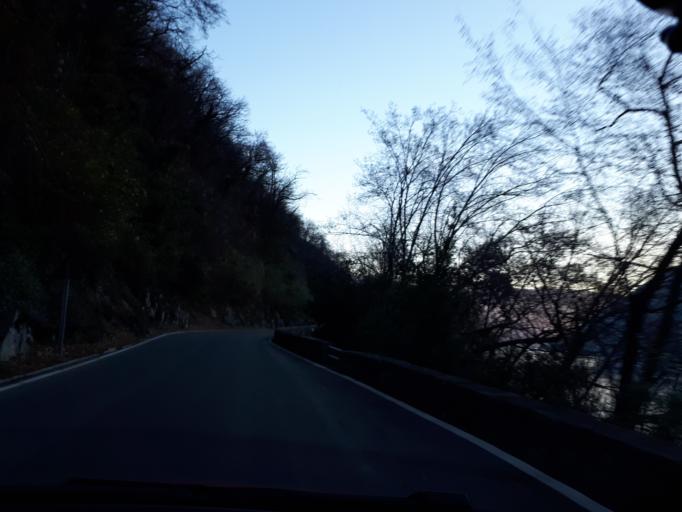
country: IT
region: Lombardy
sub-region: Provincia di Como
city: Nesso
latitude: 45.9248
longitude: 9.1512
